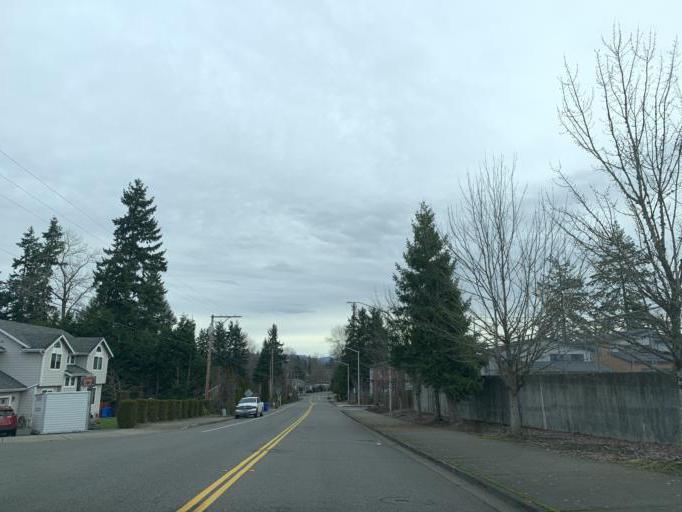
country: US
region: Washington
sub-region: King County
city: Lea Hill
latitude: 47.3598
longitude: -122.1796
